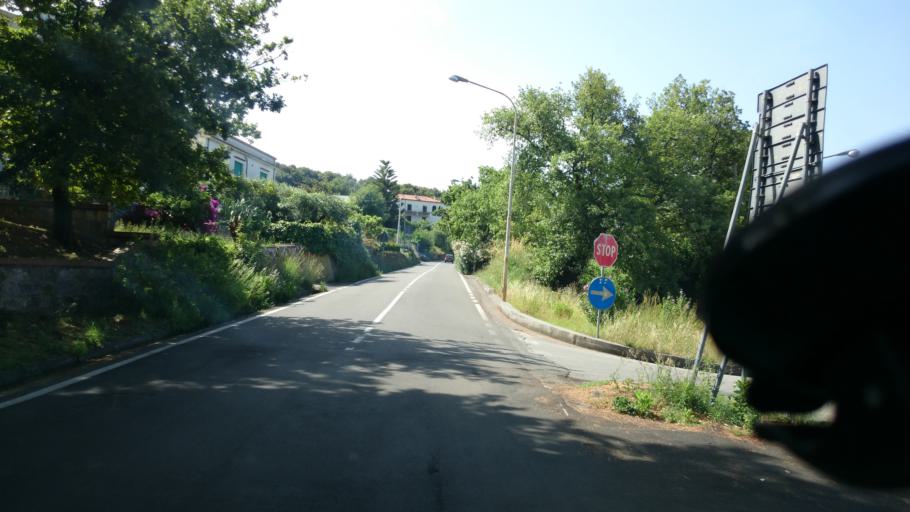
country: IT
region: Basilicate
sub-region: Provincia di Potenza
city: Maratea
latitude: 39.9969
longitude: 15.7059
